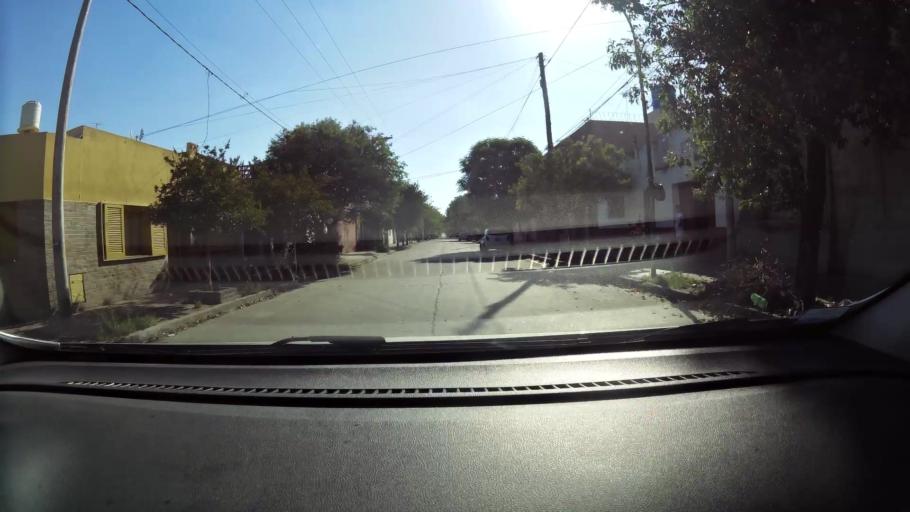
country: AR
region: Cordoba
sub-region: Departamento de Capital
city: Cordoba
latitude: -31.3994
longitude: -64.1572
